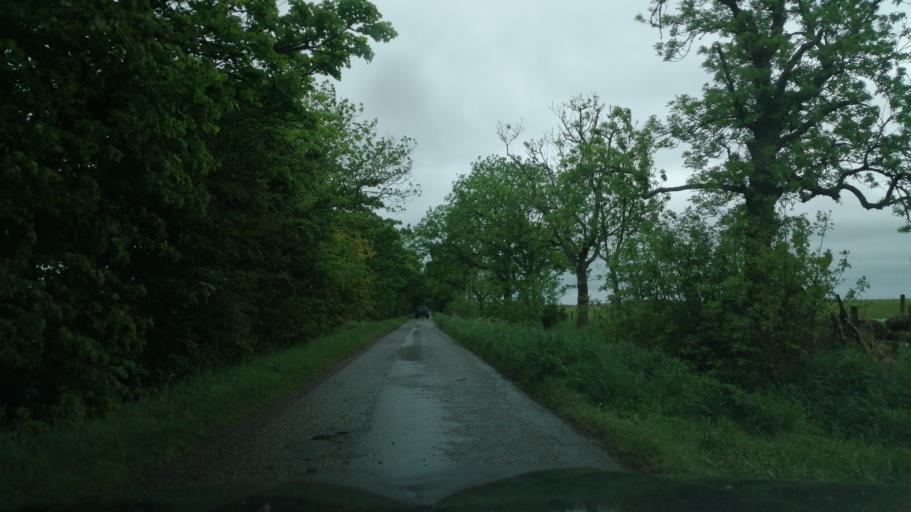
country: GB
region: Scotland
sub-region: Moray
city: Keith
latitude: 57.5706
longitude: -2.8331
